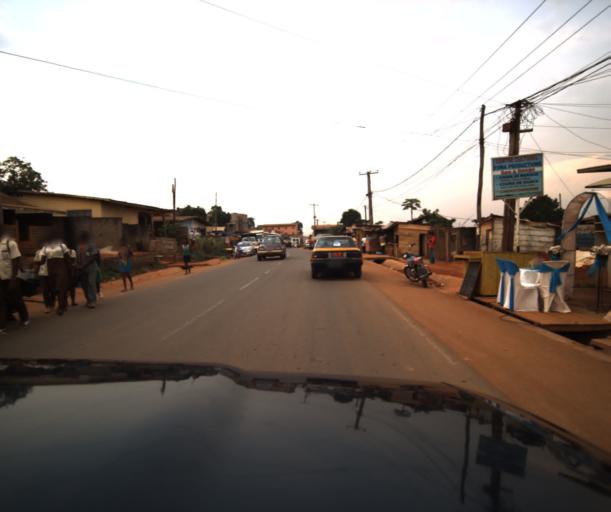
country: CM
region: Centre
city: Yaounde
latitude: 3.8354
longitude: 11.4725
